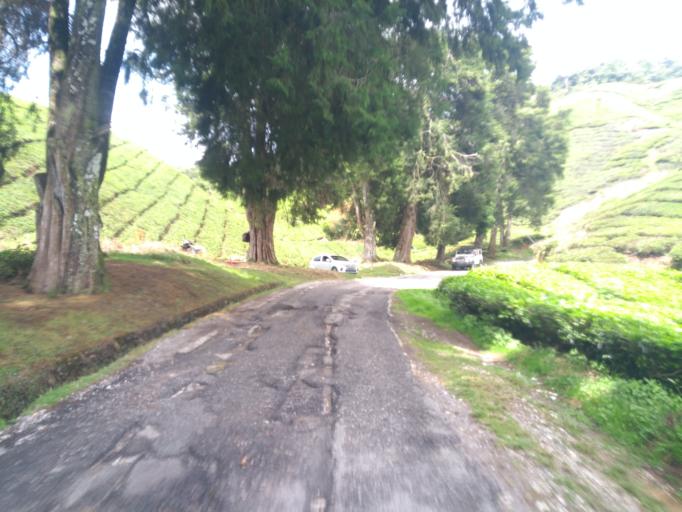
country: MY
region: Pahang
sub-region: Cameron Highlands
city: Tanah Rata
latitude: 4.5209
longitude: 101.4003
